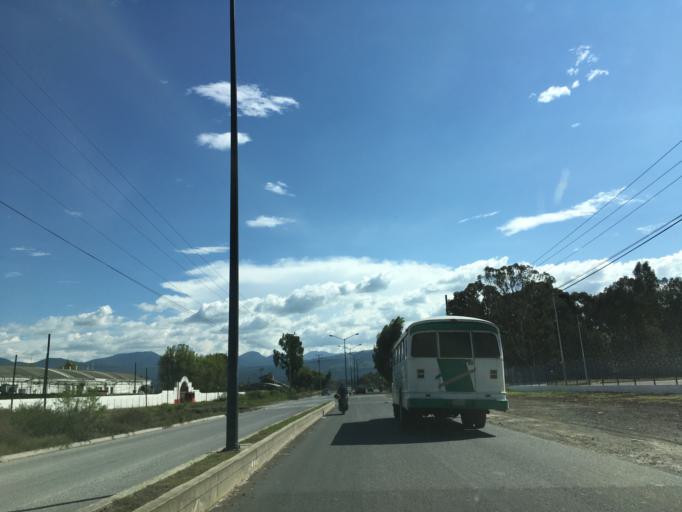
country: MX
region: Michoacan
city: Zacapu
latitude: 19.8338
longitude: -101.7709
